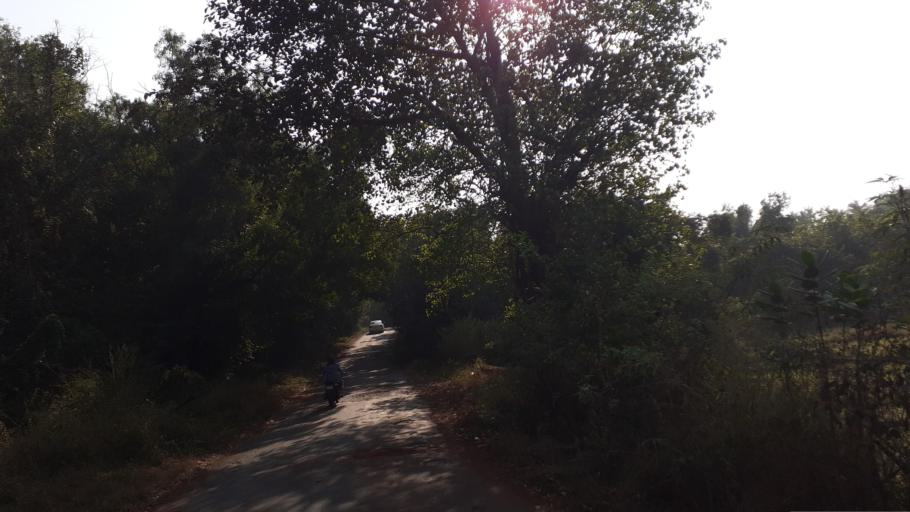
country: IN
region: Maharashtra
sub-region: Ratnagiri
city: Ratnagiri
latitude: 17.2065
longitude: 73.2488
